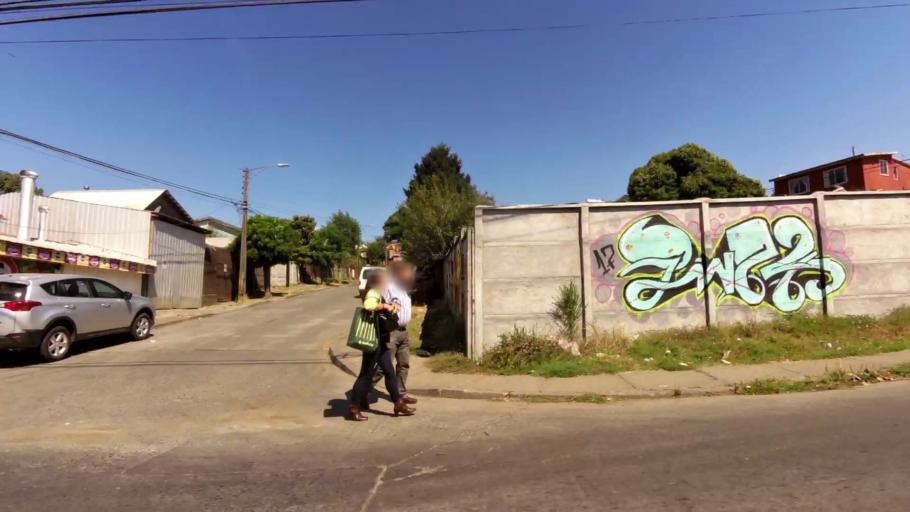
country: CL
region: Biobio
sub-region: Provincia de Concepcion
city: Concepcion
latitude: -36.8017
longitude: -73.0376
